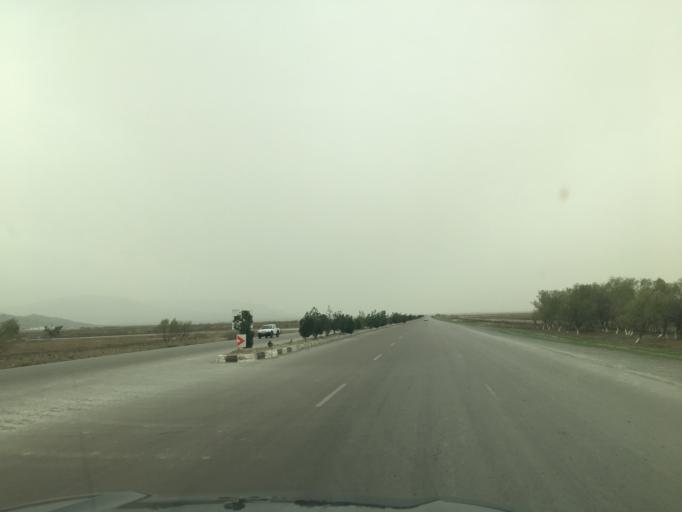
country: TM
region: Ahal
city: Baharly
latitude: 38.3480
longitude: 57.5527
